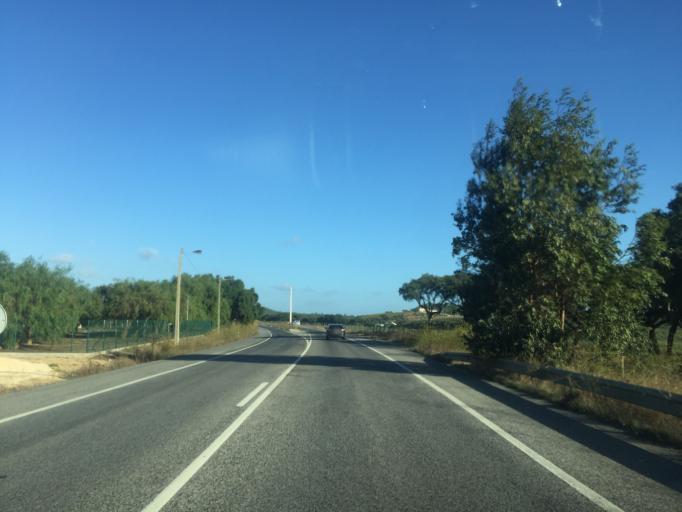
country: PT
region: Lisbon
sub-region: Azambuja
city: Alcoentre
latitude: 39.2016
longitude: -8.9532
